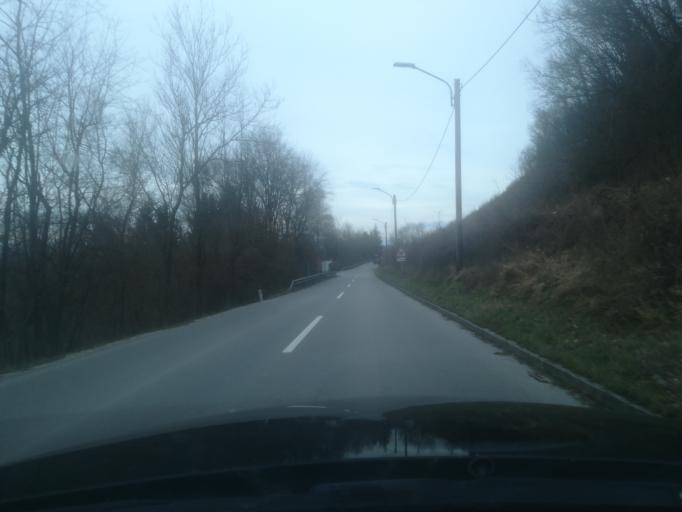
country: AT
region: Upper Austria
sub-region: Wels-Land
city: Steinhaus
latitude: 48.1375
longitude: 14.0085
